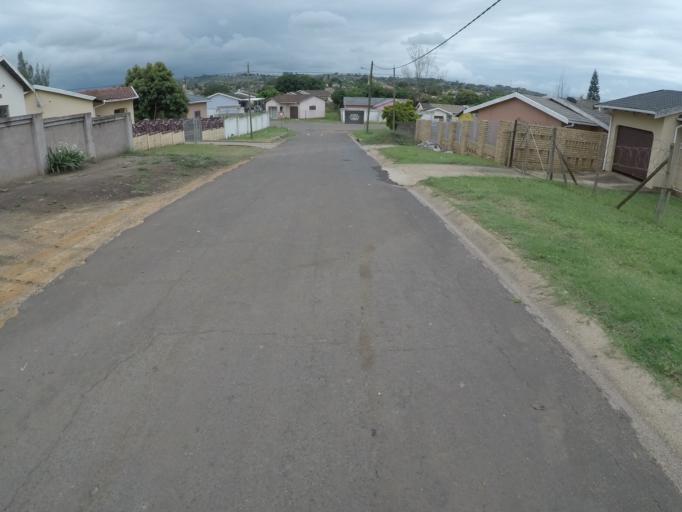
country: ZA
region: KwaZulu-Natal
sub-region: uThungulu District Municipality
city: Empangeni
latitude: -28.7832
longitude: 31.8507
